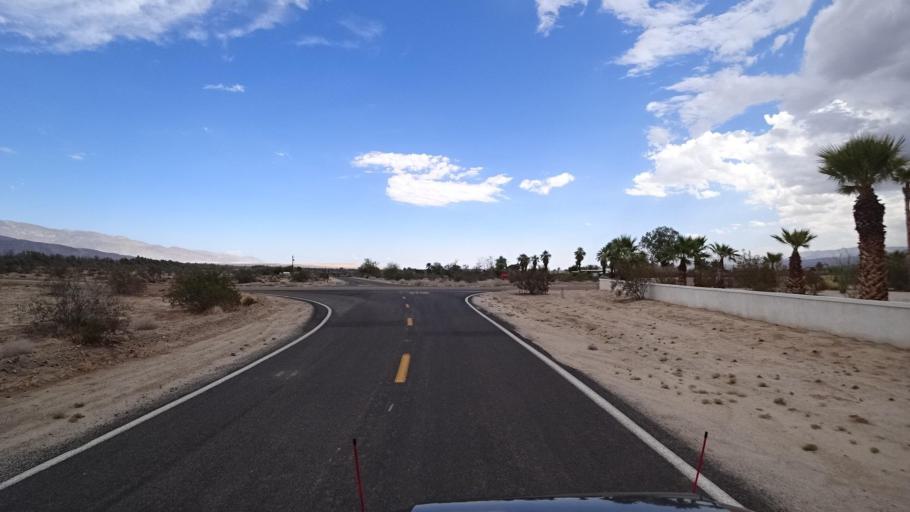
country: US
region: California
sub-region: San Diego County
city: Borrego Springs
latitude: 33.2673
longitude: -116.3862
